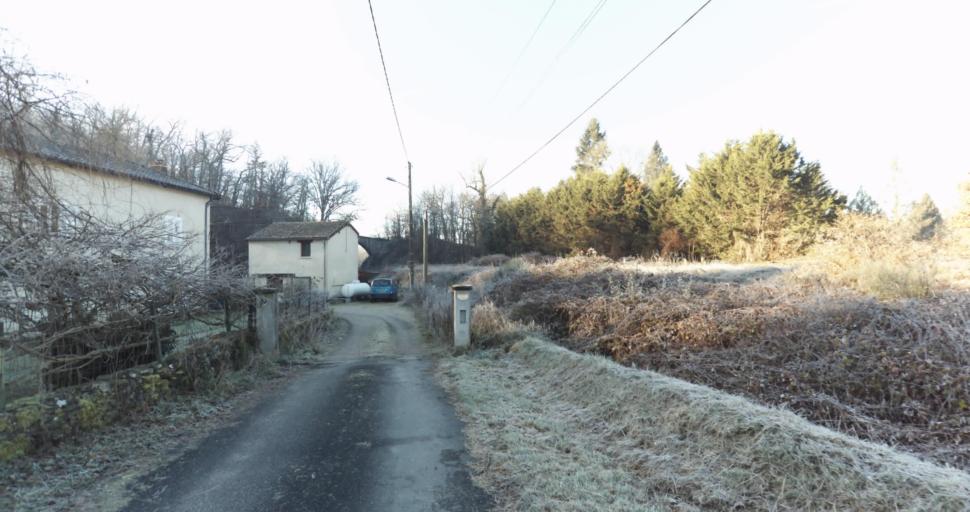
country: FR
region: Limousin
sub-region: Departement de la Haute-Vienne
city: Aixe-sur-Vienne
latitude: 45.7990
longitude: 1.1559
